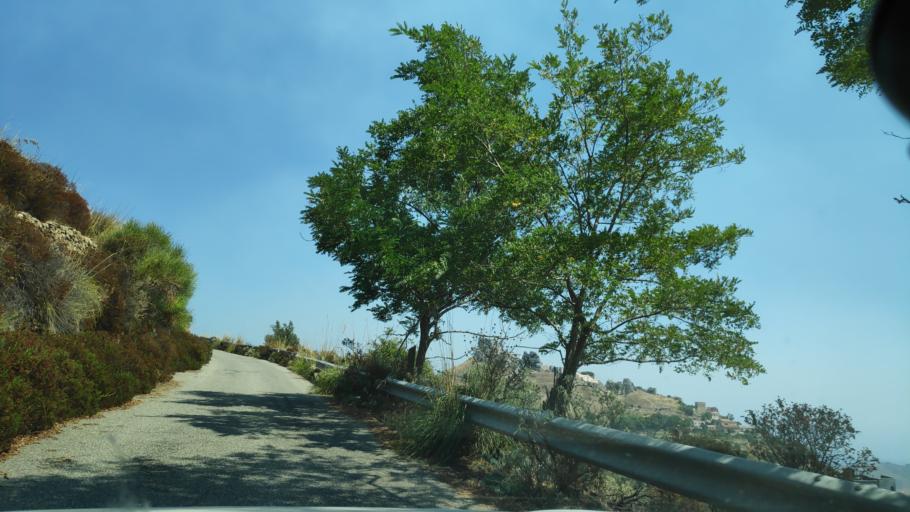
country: IT
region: Calabria
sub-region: Provincia di Reggio Calabria
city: Bova
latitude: 38.0006
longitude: 15.9238
